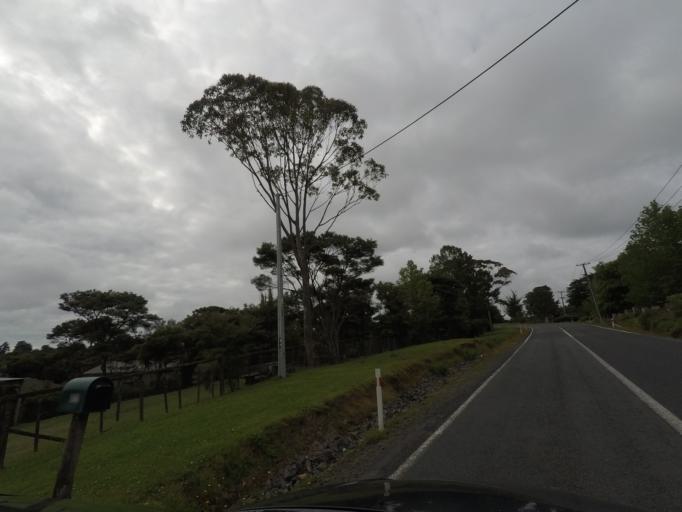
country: NZ
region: Auckland
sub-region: Auckland
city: Rosebank
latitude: -36.8343
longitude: 174.5778
